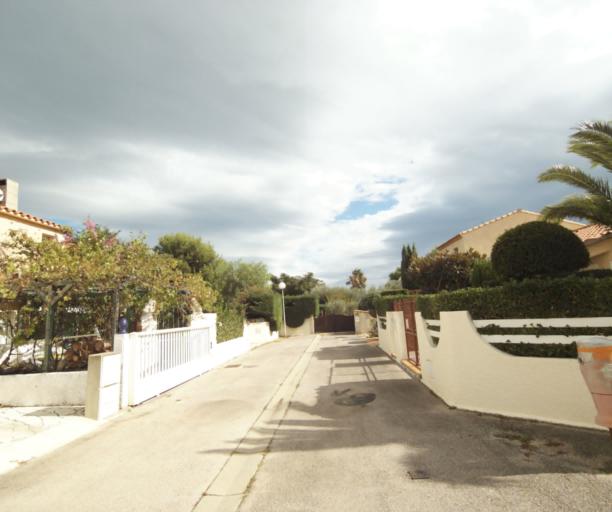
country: FR
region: Languedoc-Roussillon
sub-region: Departement des Pyrenees-Orientales
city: Argelers
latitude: 42.5520
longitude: 3.0181
